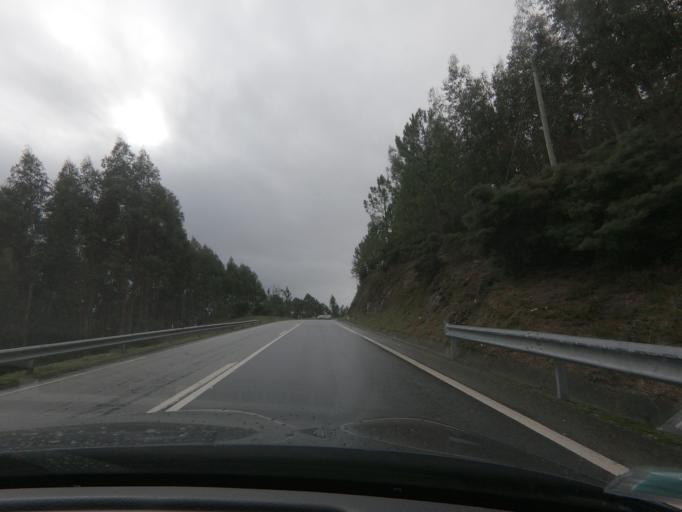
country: PT
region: Braga
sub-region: Celorico de Basto
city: Celorico de Basto
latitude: 41.3502
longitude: -8.0166
